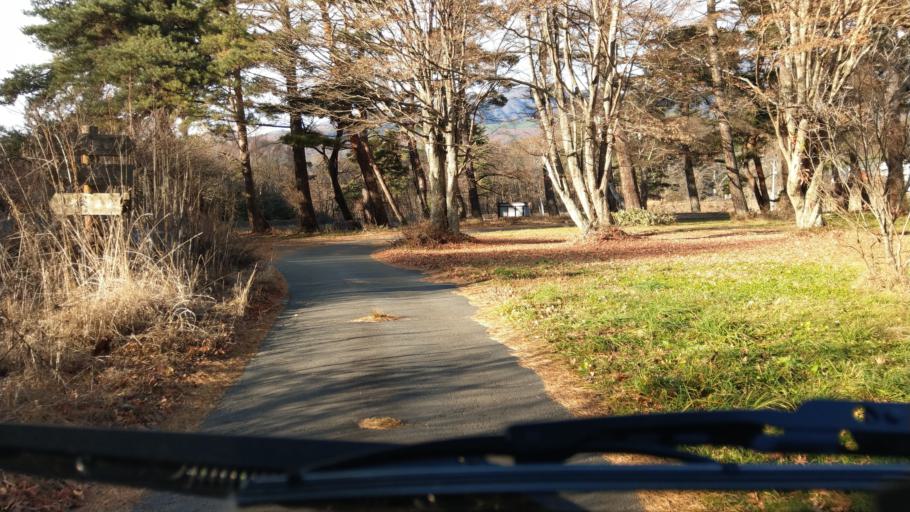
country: JP
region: Nagano
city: Komoro
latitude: 36.3461
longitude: 138.4495
